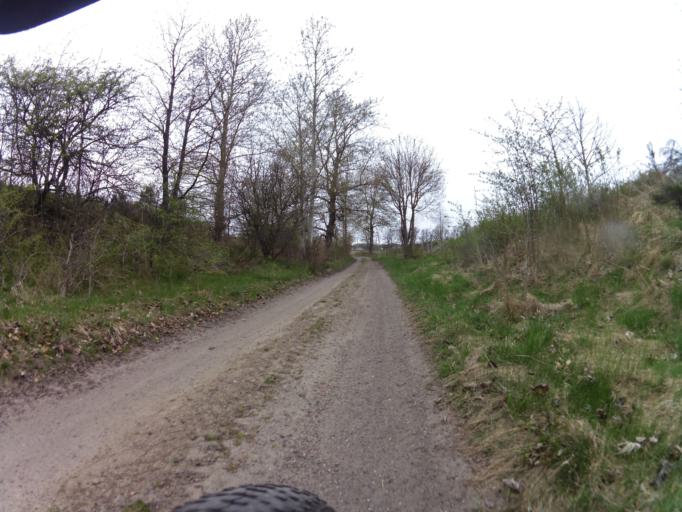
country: PL
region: West Pomeranian Voivodeship
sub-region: Powiat koszalinski
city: Bobolice
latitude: 53.9901
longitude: 16.6816
